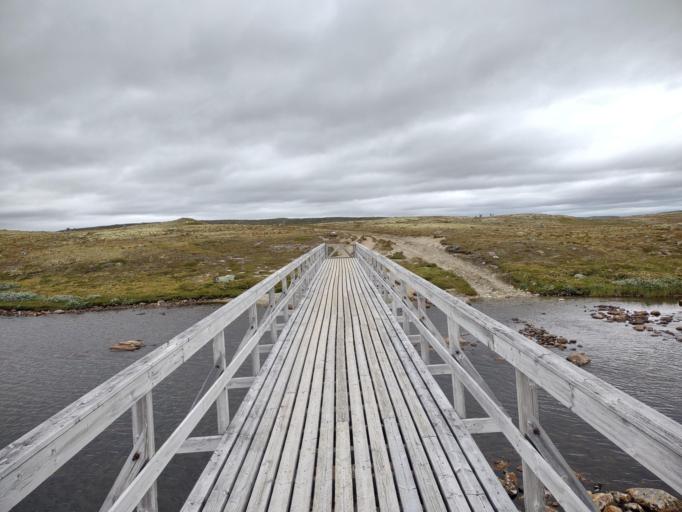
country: NO
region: Hordaland
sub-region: Eidfjord
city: Eidfjord
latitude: 60.2471
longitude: 7.5462
